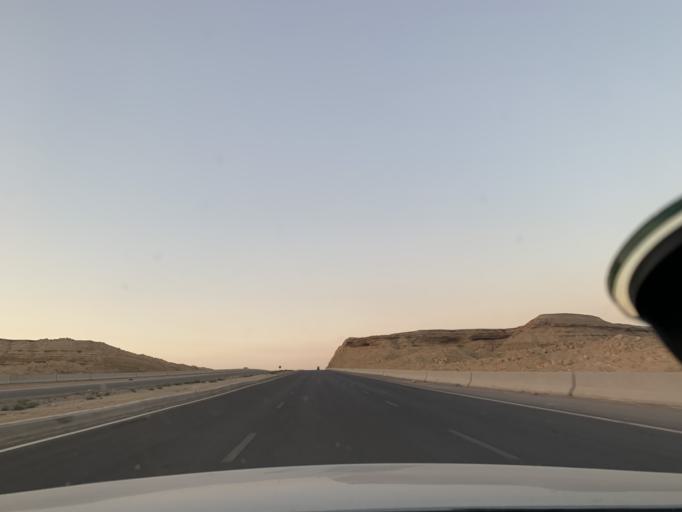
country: EG
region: Muhafazat al Qahirah
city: Halwan
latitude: 29.9477
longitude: 31.5363
